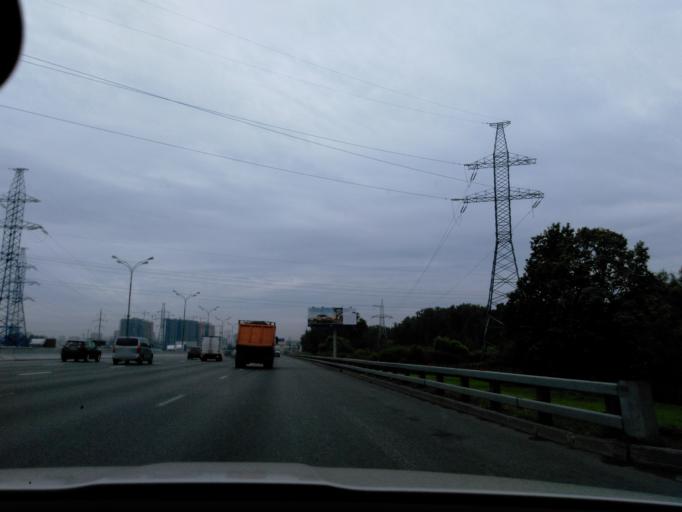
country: RU
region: Moscow
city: Ivanovskoye
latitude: 55.7889
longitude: 37.8411
